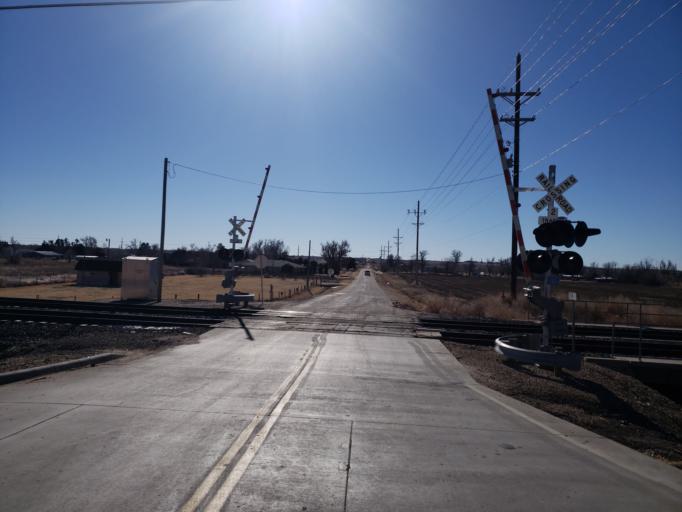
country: US
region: Kansas
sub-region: Ford County
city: Dodge City
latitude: 37.7542
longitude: -100.0513
